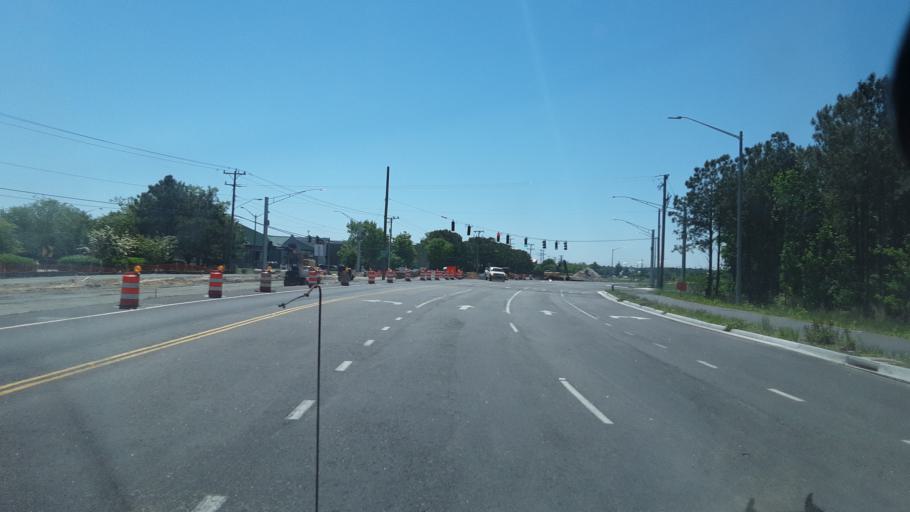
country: US
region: Virginia
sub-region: City of Virginia Beach
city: Virginia Beach
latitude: 36.7572
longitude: -76.0124
